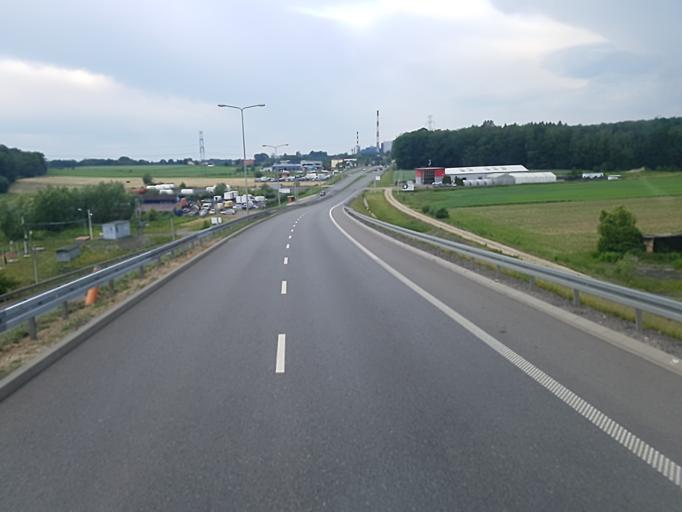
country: PL
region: Silesian Voivodeship
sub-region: Powiat pszczynski
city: Krzyzowice
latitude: 49.9586
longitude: 18.6505
